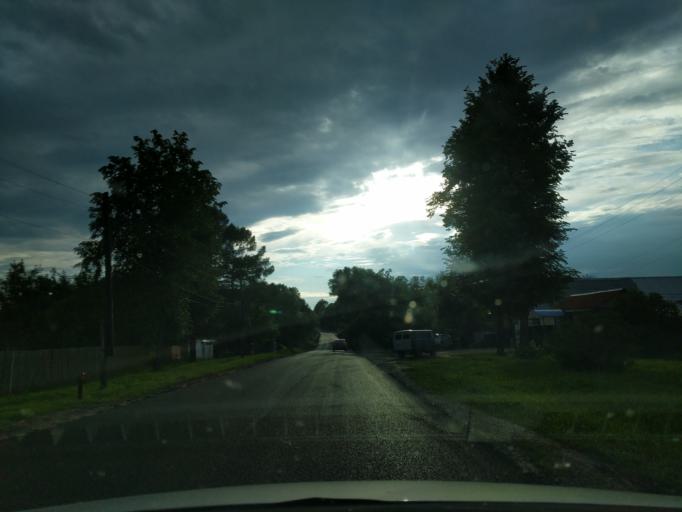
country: RU
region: Kaluga
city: Myatlevo
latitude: 54.8001
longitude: 35.7314
